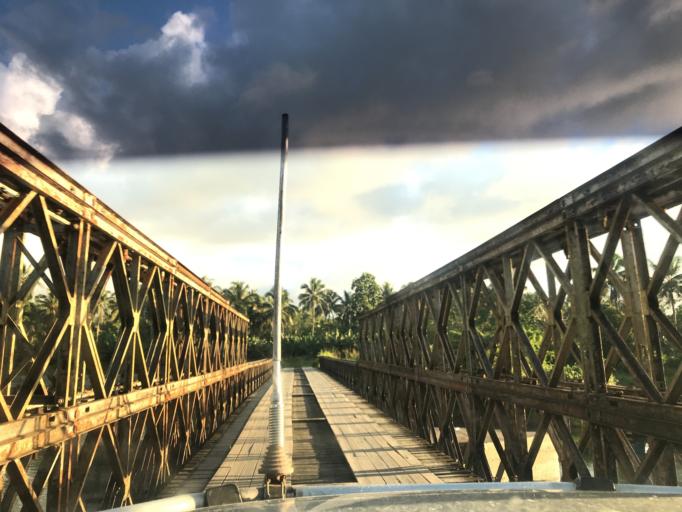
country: SB
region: Malaita
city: Auki
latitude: -8.7245
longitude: 160.7050
